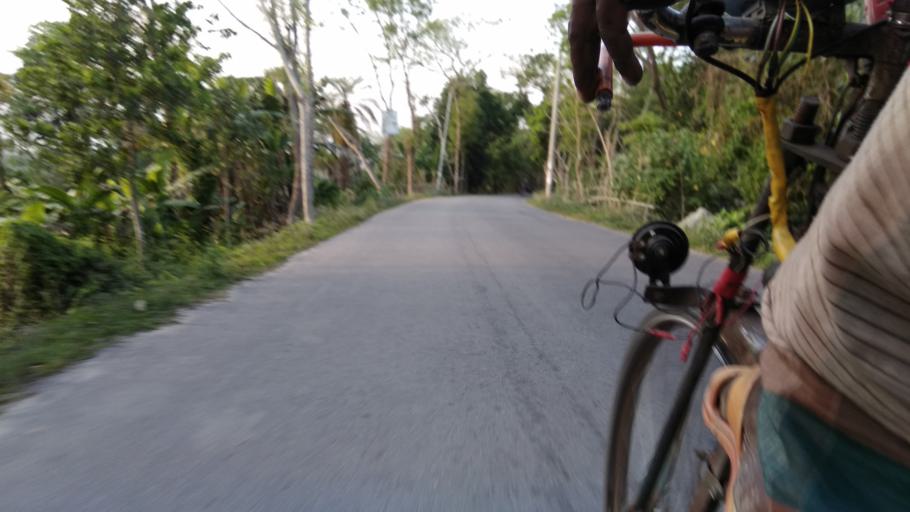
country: BD
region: Barisal
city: Mehendiganj
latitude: 22.9278
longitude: 90.4042
